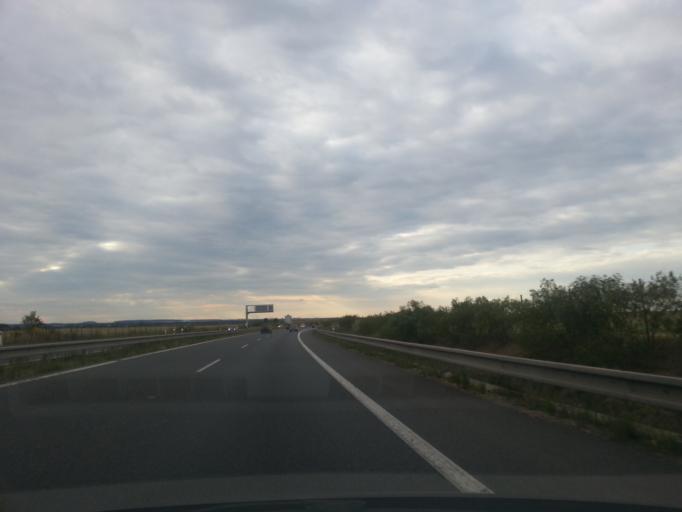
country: CZ
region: Central Bohemia
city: Hostivice
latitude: 50.0869
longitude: 14.2605
